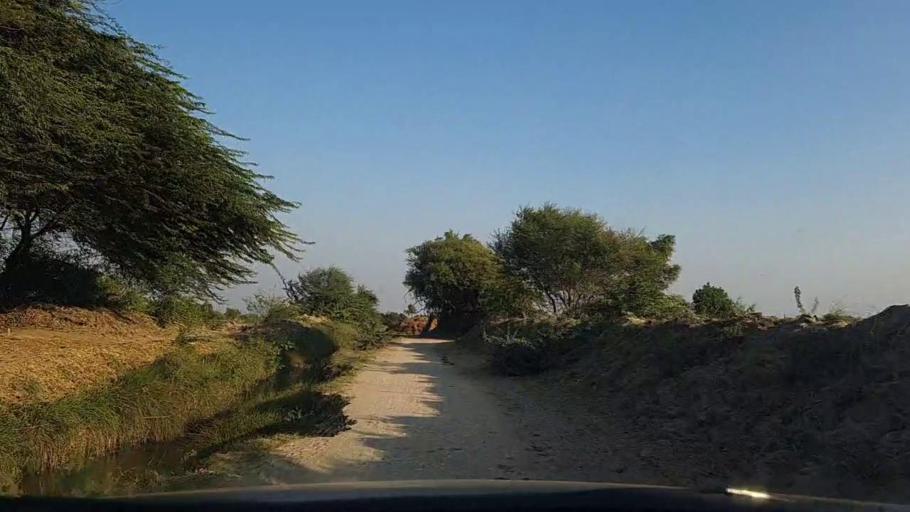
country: PK
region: Sindh
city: Mirpur Sakro
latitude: 24.5230
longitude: 67.6506
